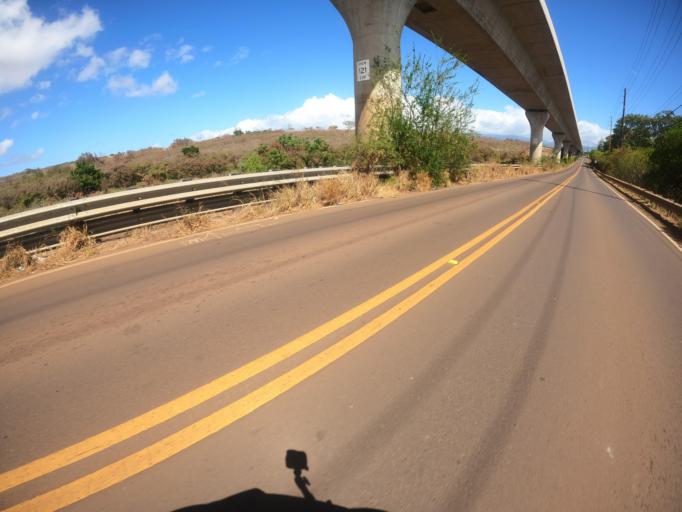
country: US
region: Hawaii
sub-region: Honolulu County
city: Royal Kunia
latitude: 21.3744
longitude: -158.0350
